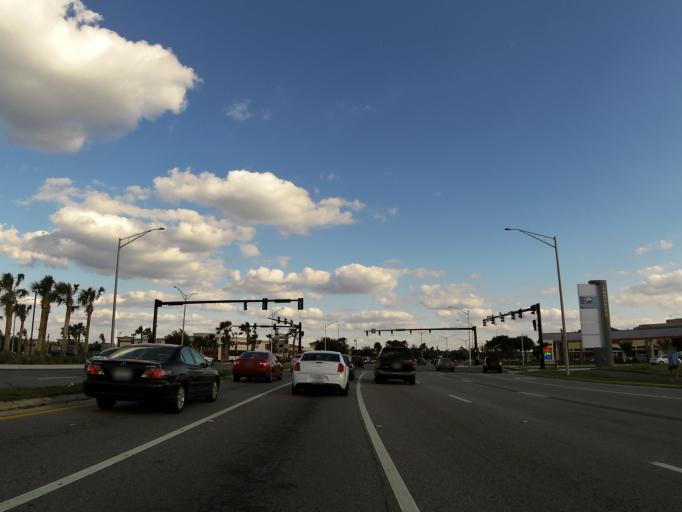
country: US
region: Florida
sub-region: Duval County
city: Jacksonville
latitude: 30.2552
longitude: -81.5367
